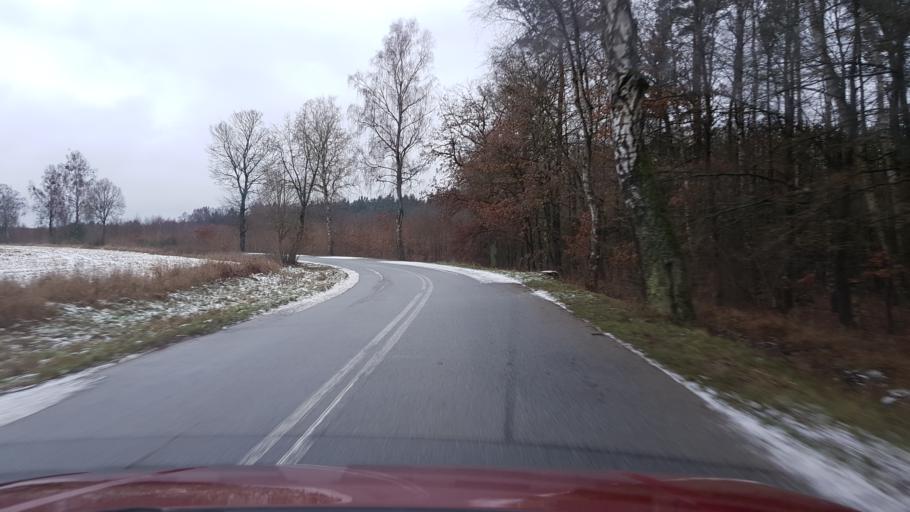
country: PL
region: West Pomeranian Voivodeship
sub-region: Powiat lobeski
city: Resko
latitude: 53.8178
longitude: 15.3963
